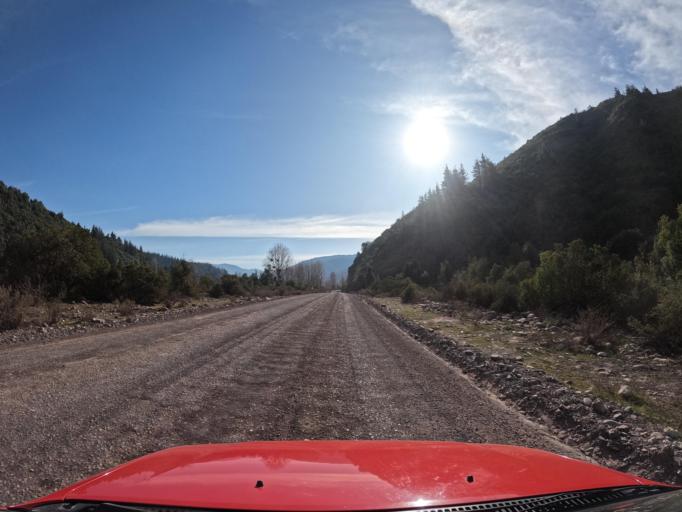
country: CL
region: O'Higgins
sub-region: Provincia de Colchagua
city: Chimbarongo
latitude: -34.9991
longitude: -70.8025
